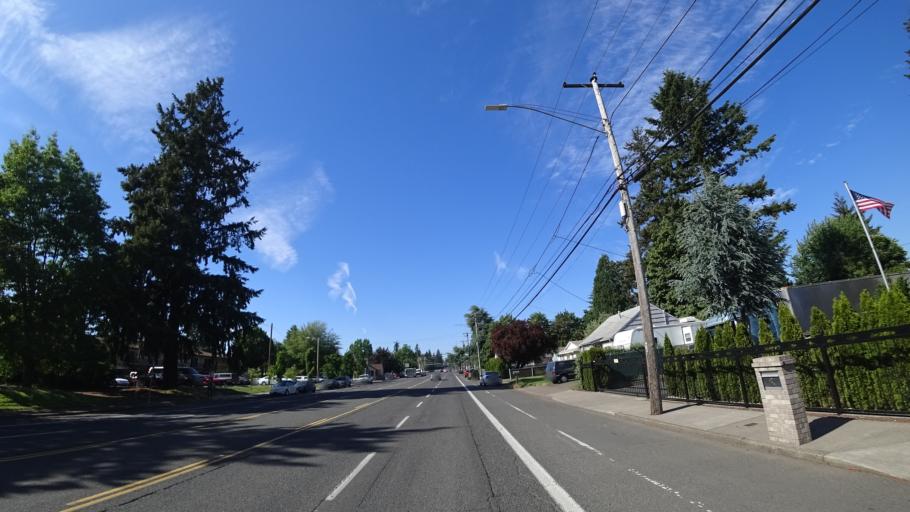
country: US
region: Oregon
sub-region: Multnomah County
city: Fairview
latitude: 45.5165
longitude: -122.4964
